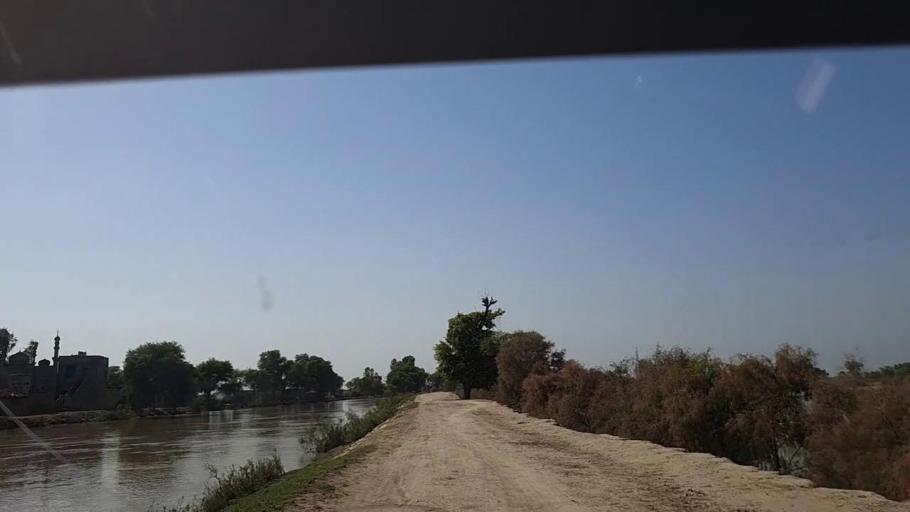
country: PK
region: Sindh
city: Ghauspur
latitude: 28.1802
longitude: 69.0878
